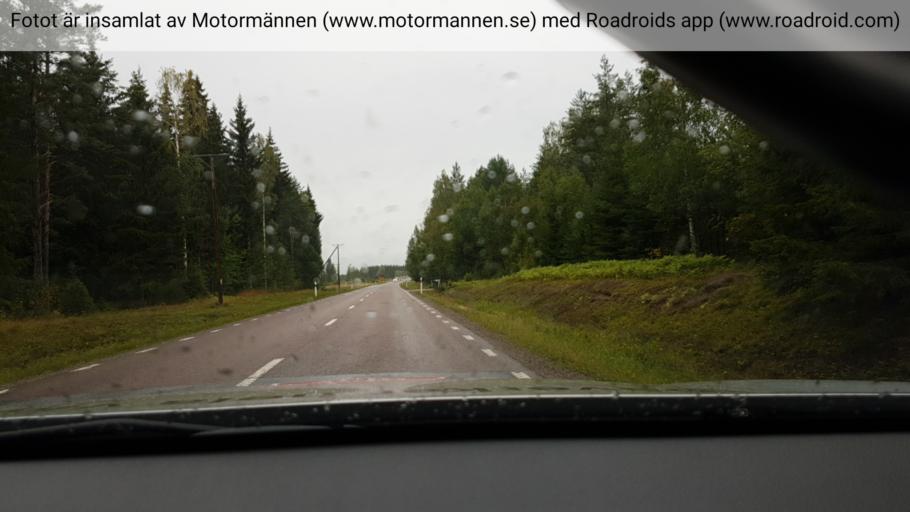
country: SE
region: Gaevleborg
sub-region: Gavle Kommun
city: Hedesunda
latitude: 60.4808
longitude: 16.9390
